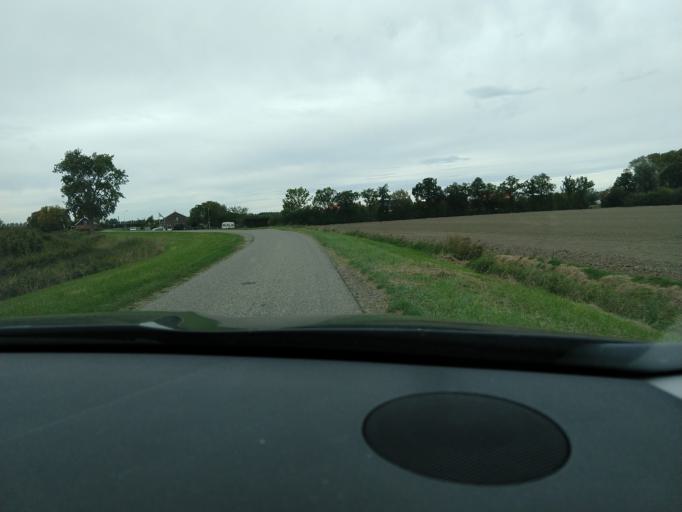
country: NL
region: Zeeland
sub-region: Gemeente Borsele
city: Borssele
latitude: 51.4125
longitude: 3.7995
